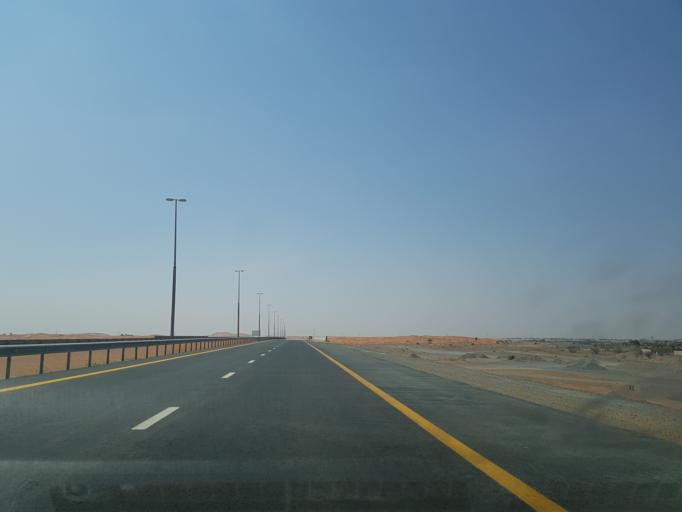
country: AE
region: Ash Shariqah
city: Adh Dhayd
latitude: 25.2386
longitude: 55.8919
